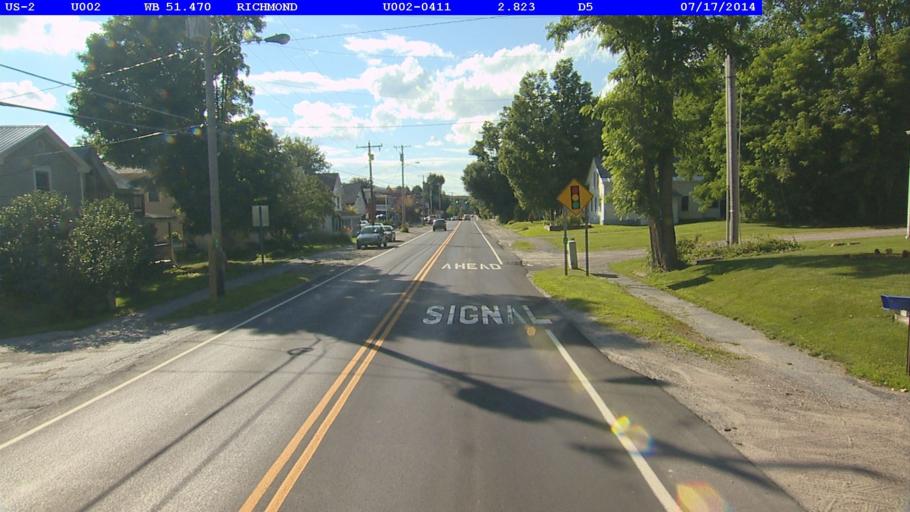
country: US
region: Vermont
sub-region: Chittenden County
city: Williston
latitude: 44.4043
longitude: -72.9913
